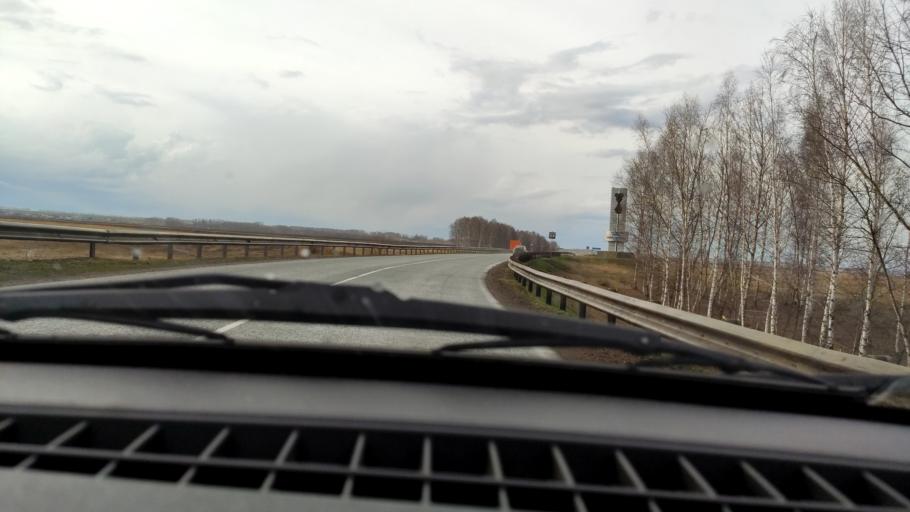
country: RU
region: Bashkortostan
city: Alekseyevka
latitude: 55.0798
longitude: 55.0672
